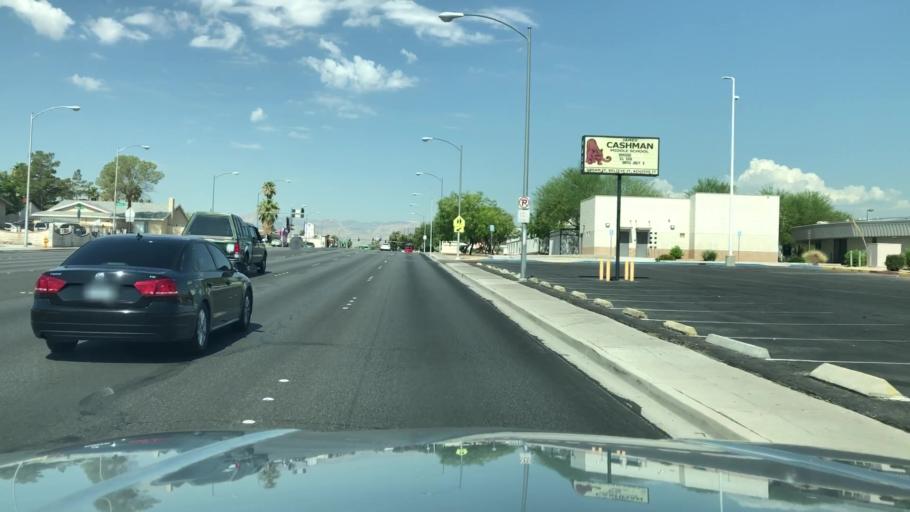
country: US
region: Nevada
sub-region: Clark County
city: Spring Valley
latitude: 36.1301
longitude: -115.2040
